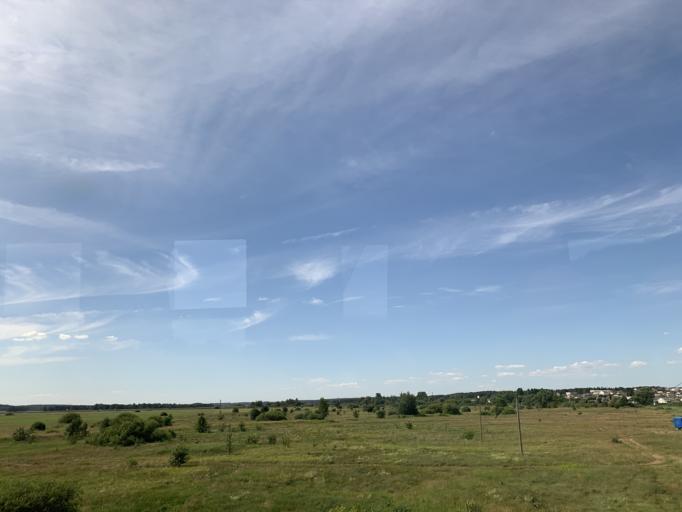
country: BY
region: Minsk
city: Novy Svyerzhan'
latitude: 53.4695
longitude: 26.7279
